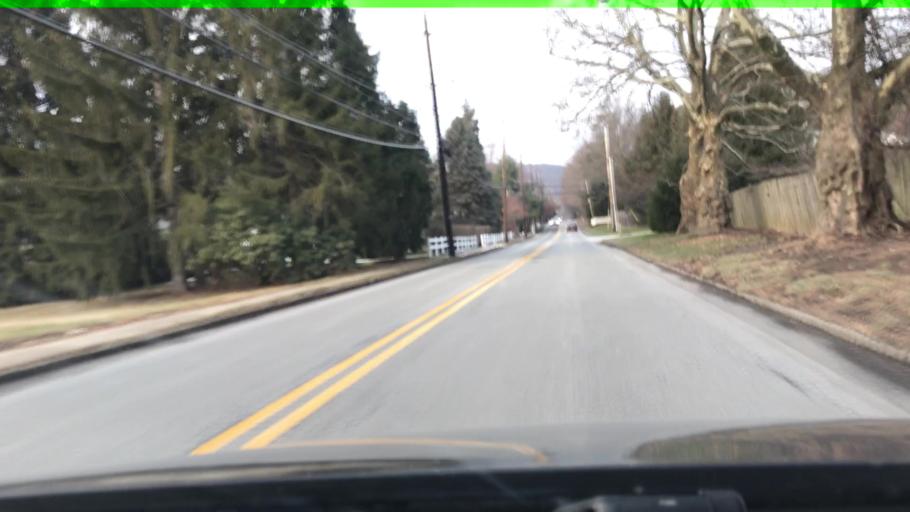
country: US
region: New Jersey
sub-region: Morris County
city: Mendham
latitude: 40.7852
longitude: -74.5853
